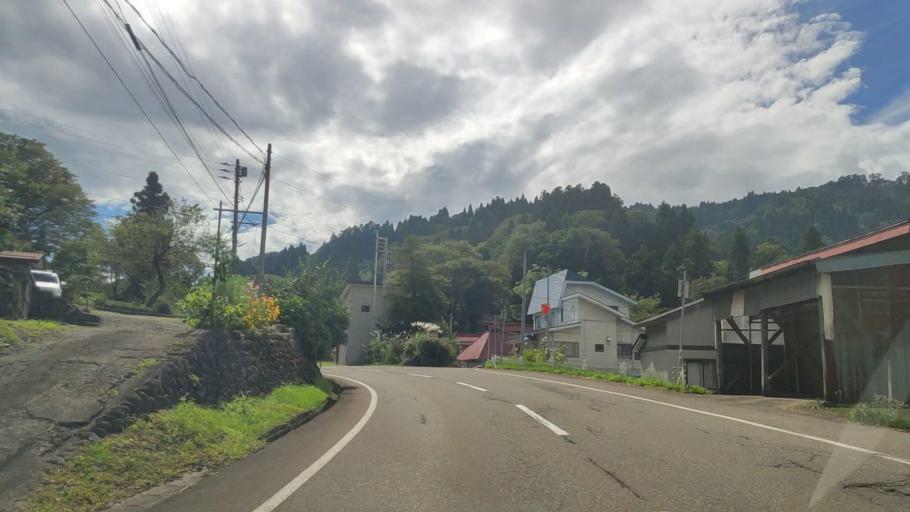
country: JP
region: Niigata
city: Arai
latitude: 36.9294
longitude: 138.2983
